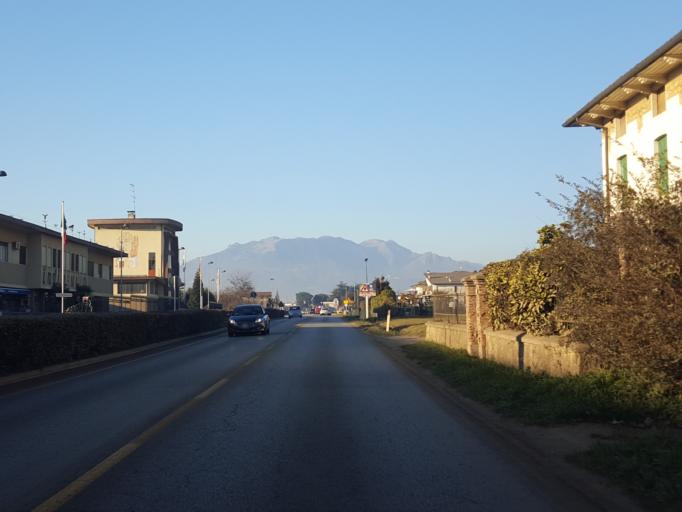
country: IT
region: Veneto
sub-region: Provincia di Vicenza
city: Malo
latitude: 45.6466
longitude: 11.4251
